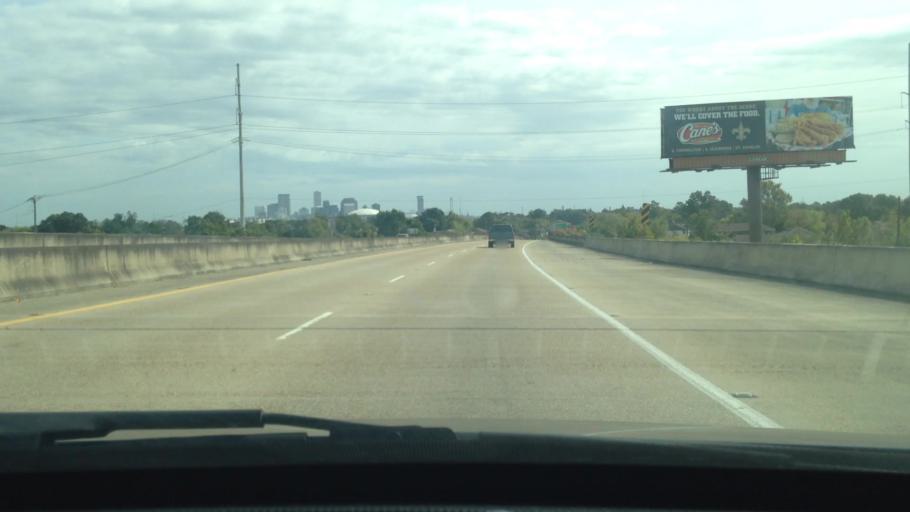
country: US
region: Louisiana
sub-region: Jefferson Parish
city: Jefferson
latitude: 29.9682
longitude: -90.1301
